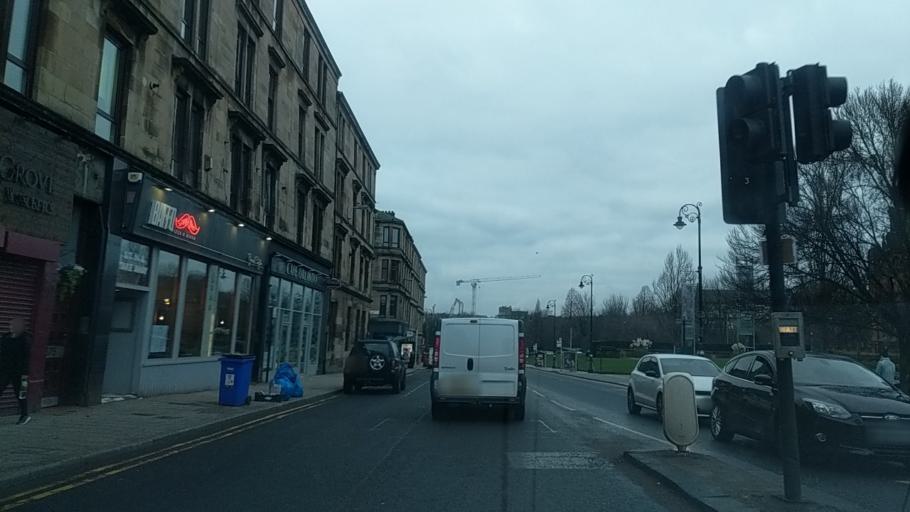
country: GB
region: Scotland
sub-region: Glasgow City
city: Glasgow
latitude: 55.8677
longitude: -4.2913
